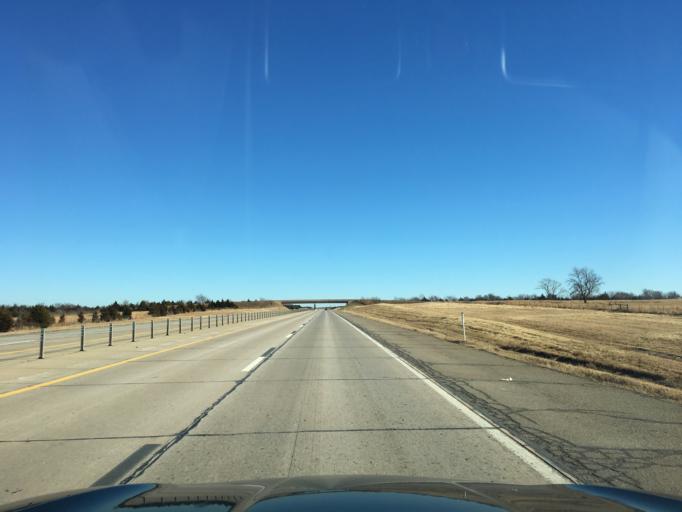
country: US
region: Oklahoma
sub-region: Pawnee County
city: Pawnee
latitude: 36.2250
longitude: -96.8416
